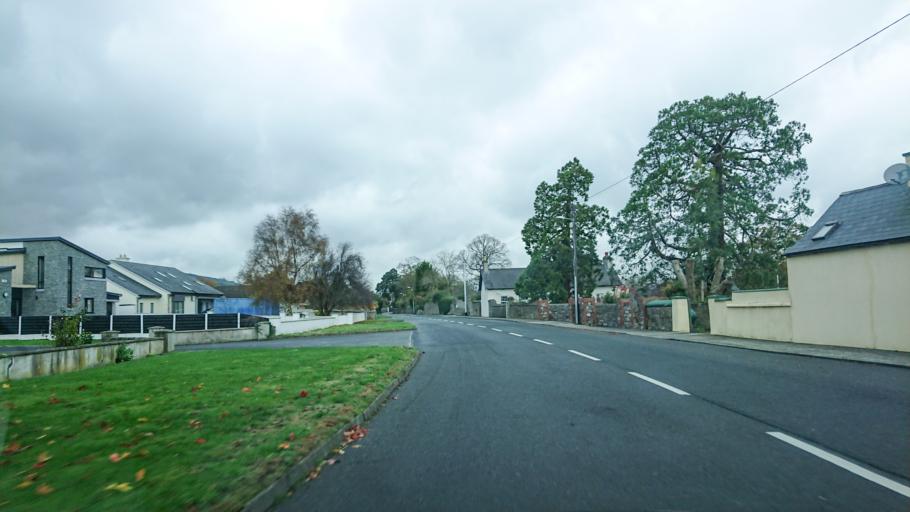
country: IE
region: Munster
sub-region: South Tipperary
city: Cluain Meala
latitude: 52.3528
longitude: -7.6789
